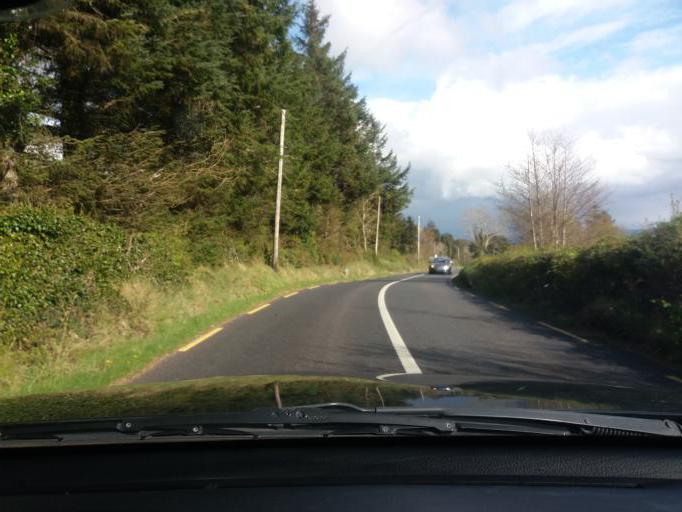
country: IE
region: Connaught
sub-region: County Leitrim
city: Kinlough
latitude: 54.3723
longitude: -8.2739
